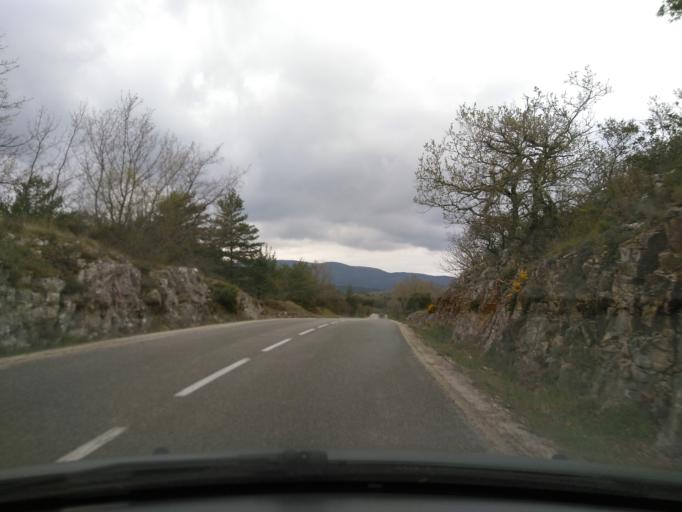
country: FR
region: Languedoc-Roussillon
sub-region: Departement du Gard
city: Barjac
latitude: 44.3587
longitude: 4.3735
